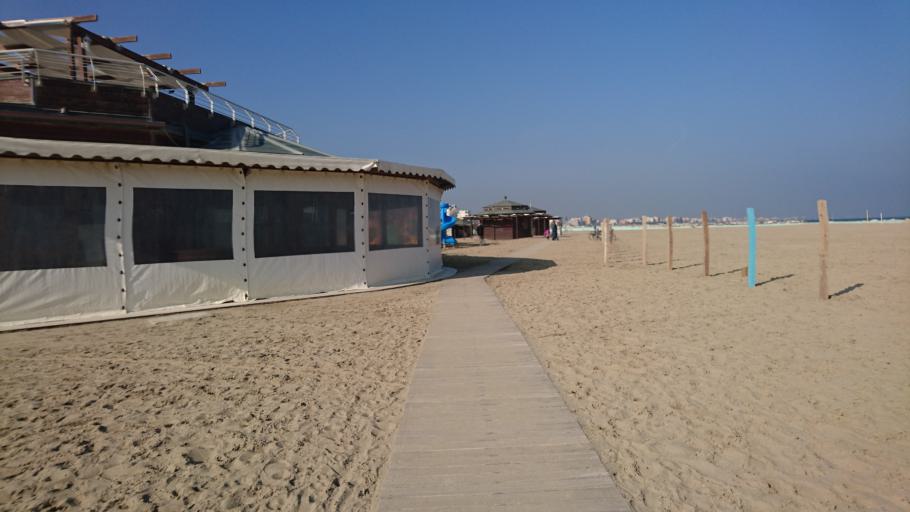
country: IT
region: Emilia-Romagna
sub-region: Provincia di Rimini
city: Rimini
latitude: 44.0756
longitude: 12.5658
